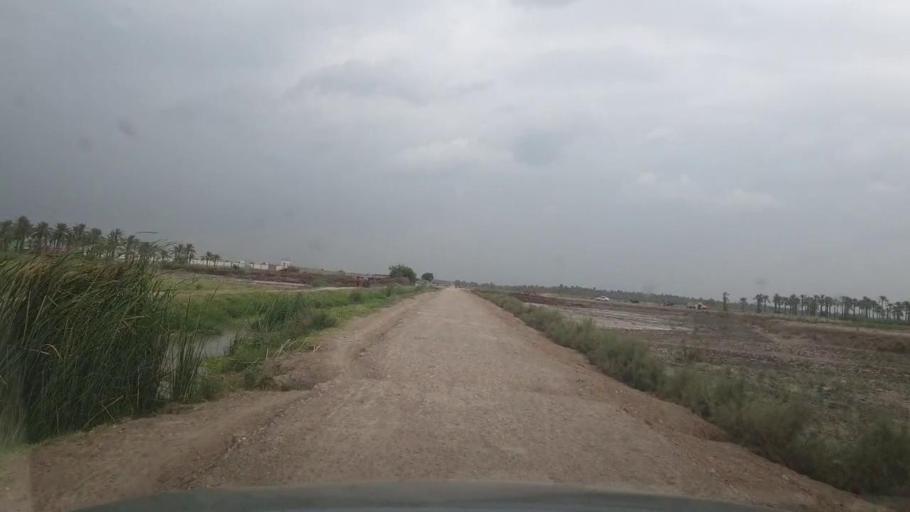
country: PK
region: Sindh
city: Khairpur
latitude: 27.5524
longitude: 68.6924
